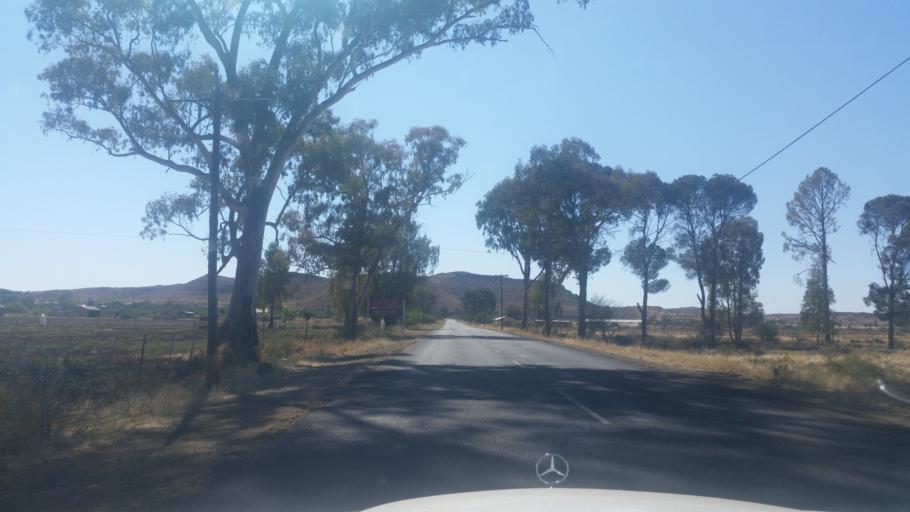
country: ZA
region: Orange Free State
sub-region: Xhariep District Municipality
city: Trompsburg
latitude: -30.4964
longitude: 25.9896
